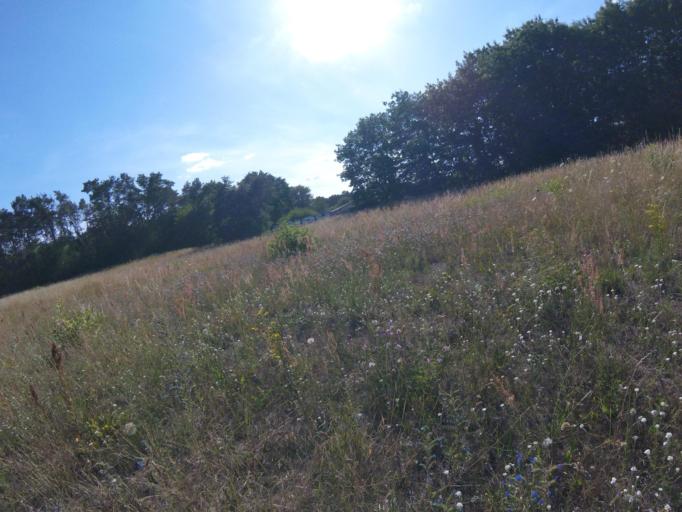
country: DE
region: Brandenburg
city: Konigs Wusterhausen
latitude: 52.3079
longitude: 13.6839
